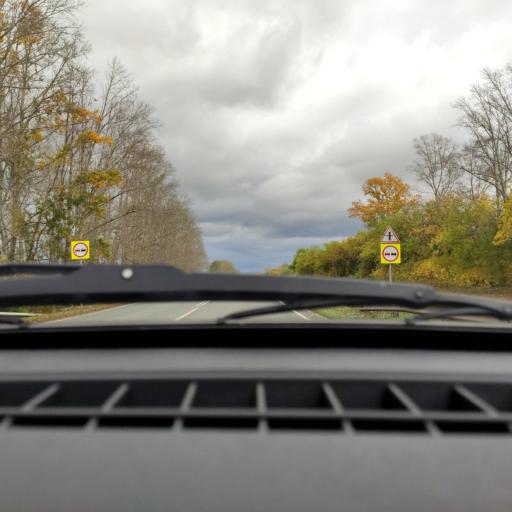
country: RU
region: Bashkortostan
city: Shafranovo
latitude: 54.0142
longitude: 54.8189
